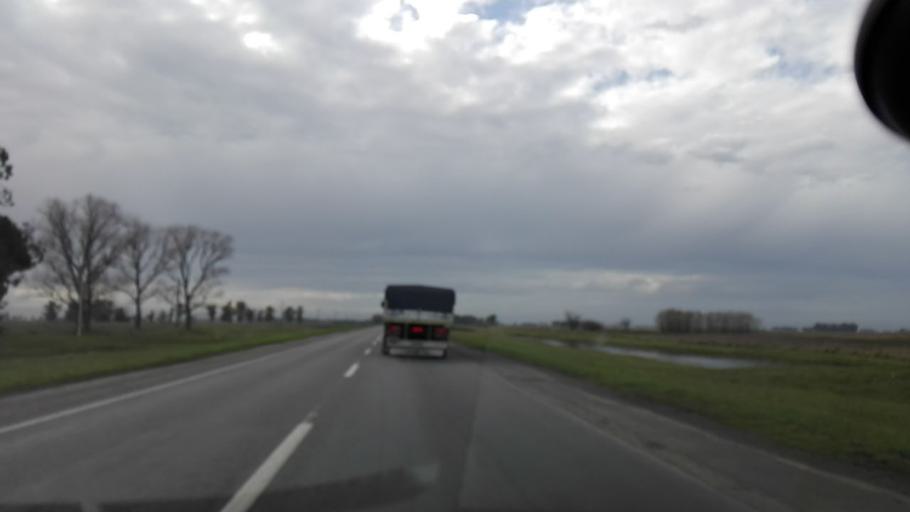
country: AR
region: Buenos Aires
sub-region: Partido de Las Flores
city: Las Flores
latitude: -35.9665
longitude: -59.0248
